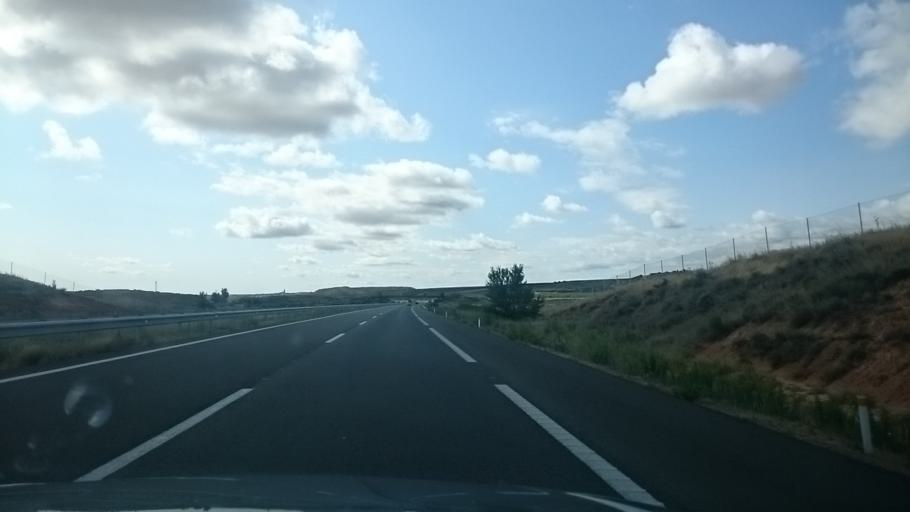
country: ES
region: Navarre
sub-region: Provincia de Navarra
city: Azagra
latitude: 42.2717
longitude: -1.9317
